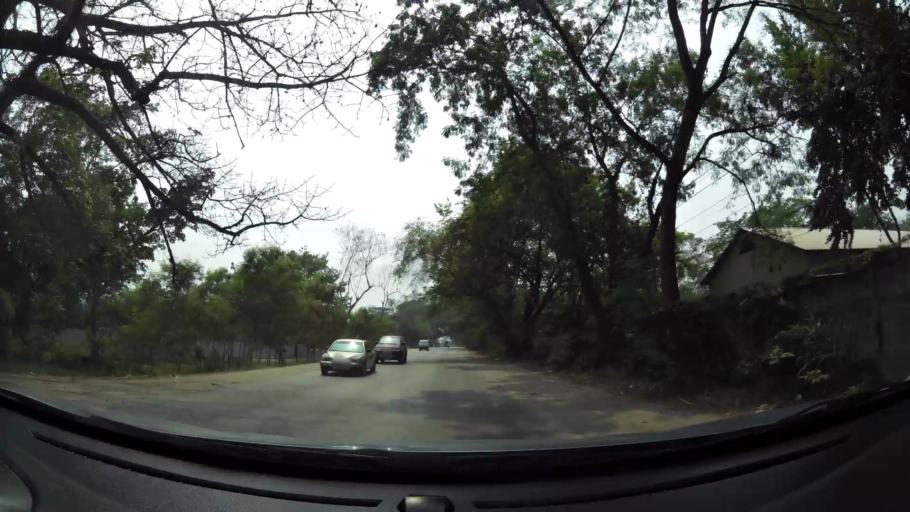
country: HN
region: Cortes
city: Chotepe
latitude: 15.4648
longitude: -87.9726
